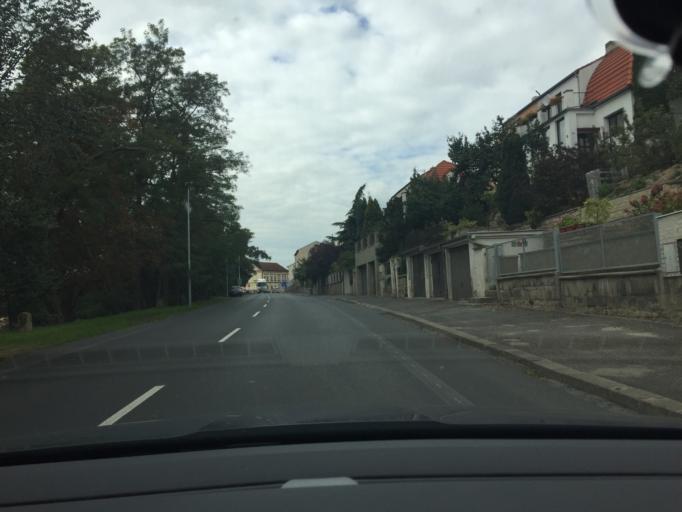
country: CZ
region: Ustecky
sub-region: Okres Litomerice
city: Litomerice
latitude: 50.5340
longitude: 14.1459
